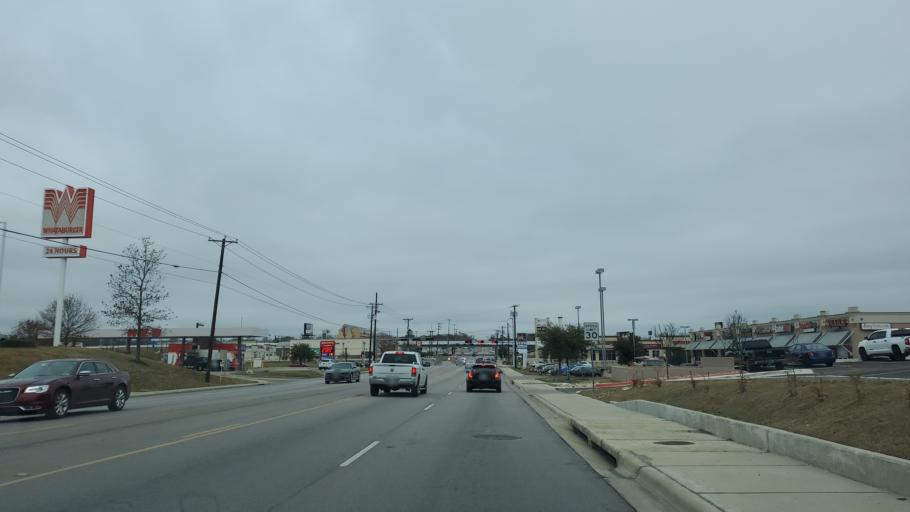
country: US
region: Texas
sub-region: Bell County
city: Killeen
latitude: 31.0910
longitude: -97.7336
